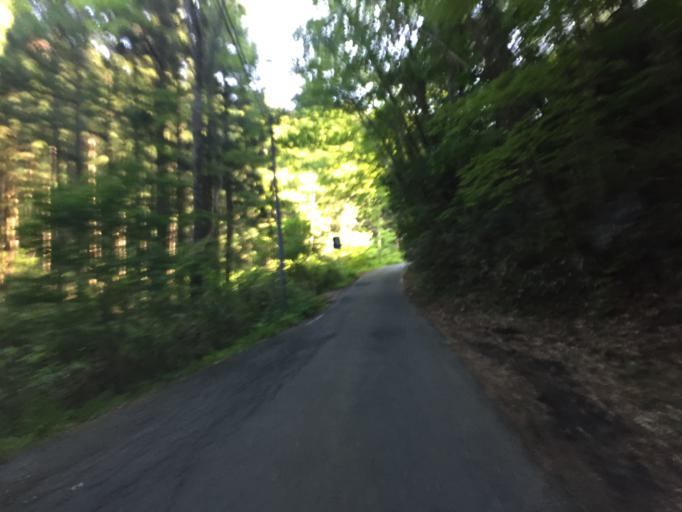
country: JP
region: Ibaraki
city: Kitaibaraki
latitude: 36.8941
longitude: 140.6106
